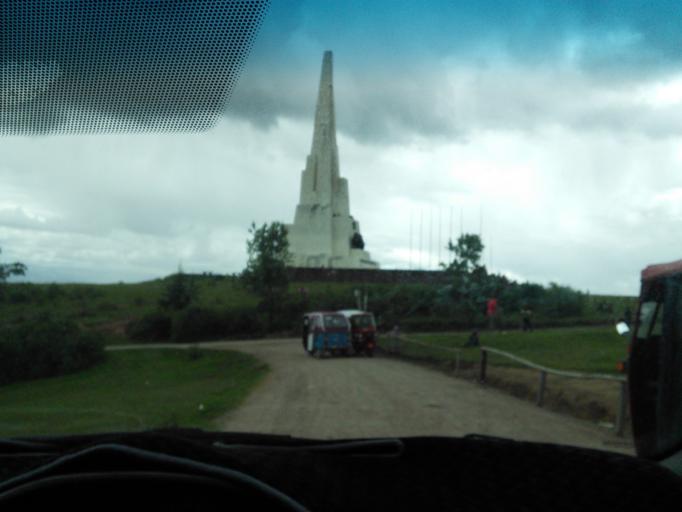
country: PE
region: Ayacucho
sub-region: Provincia de Huamanga
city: Quinua
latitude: -13.0427
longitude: -74.1305
